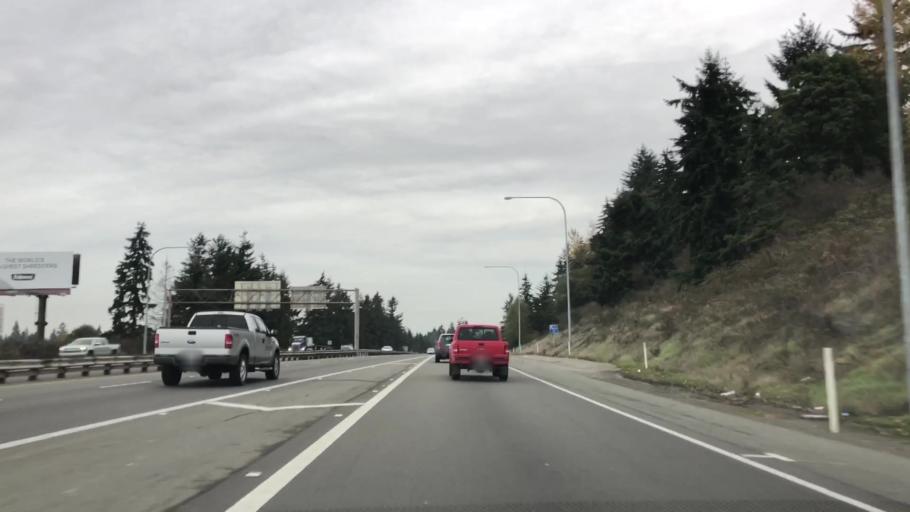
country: US
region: Washington
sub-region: King County
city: Burien
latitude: 47.4751
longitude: -122.3297
